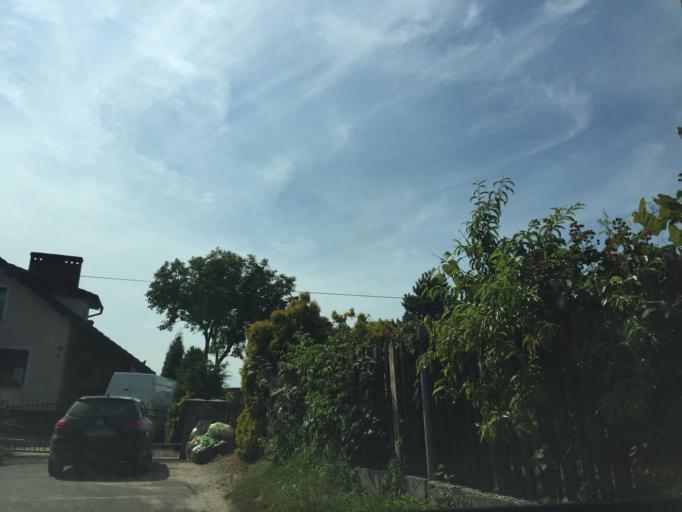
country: PL
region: Silesian Voivodeship
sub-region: Powiat wodzislawski
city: Gorzyce
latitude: 49.9607
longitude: 18.3972
